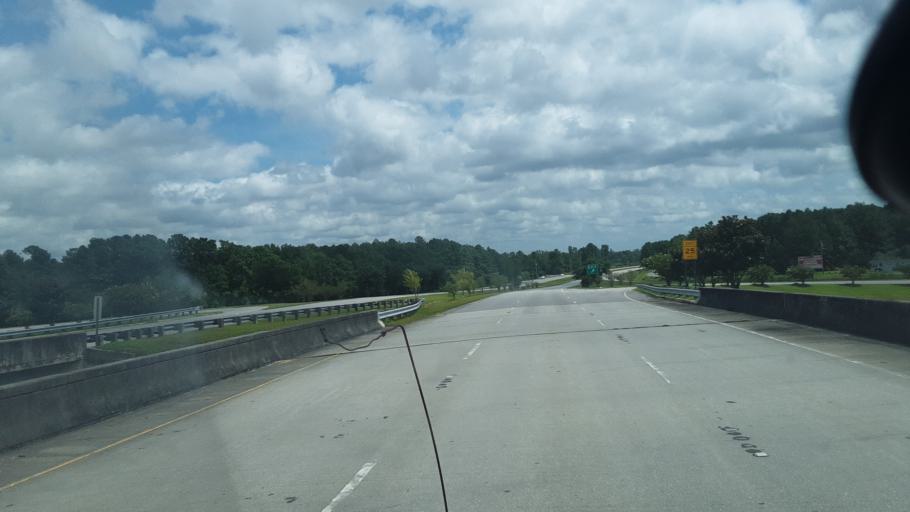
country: US
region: South Carolina
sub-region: Horry County
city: Loris
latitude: 34.0825
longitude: -78.8748
